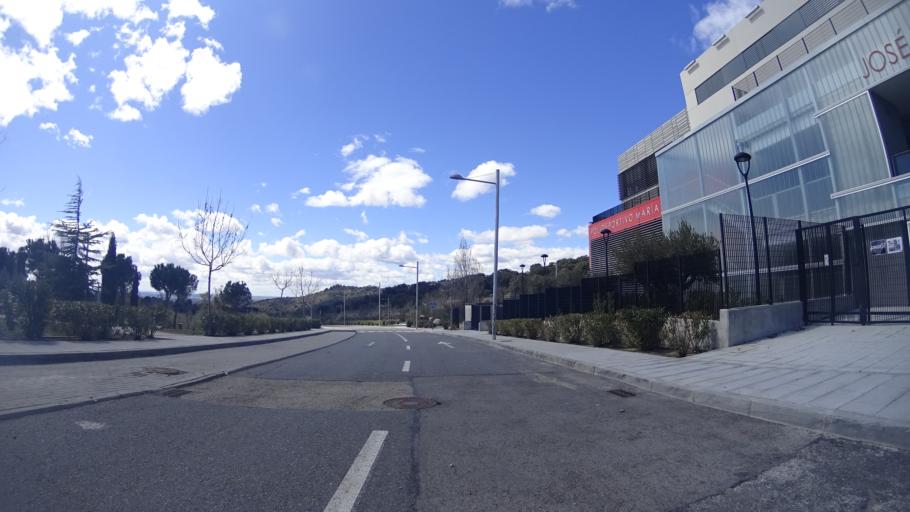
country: ES
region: Madrid
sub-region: Provincia de Madrid
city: Torrelodones
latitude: 40.5674
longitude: -3.9238
